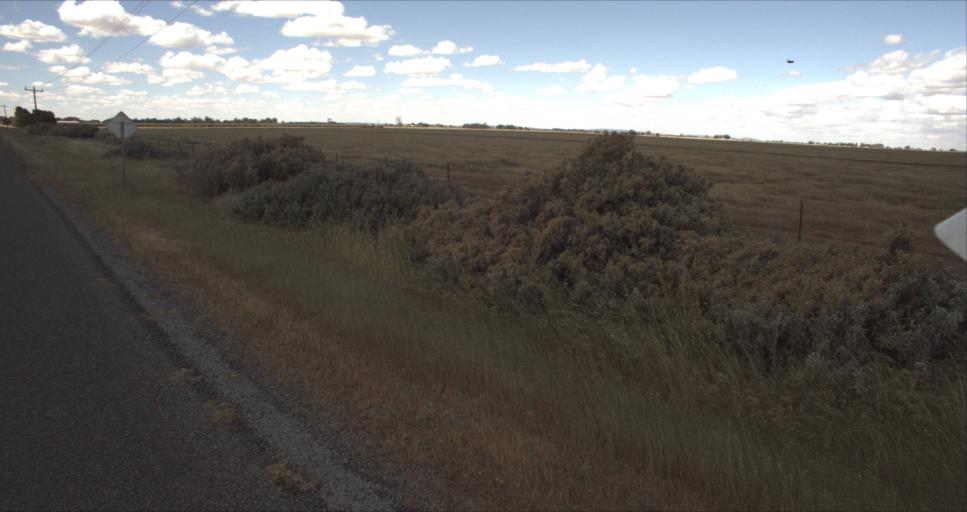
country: AU
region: New South Wales
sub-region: Leeton
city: Leeton
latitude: -34.5295
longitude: 146.2190
